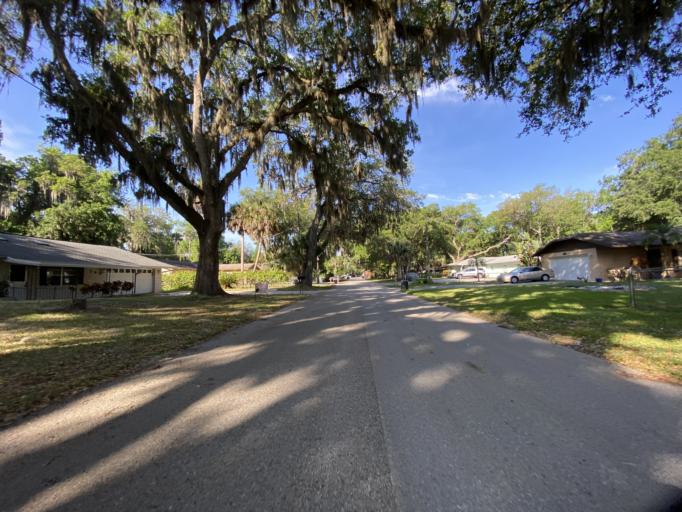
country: US
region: Florida
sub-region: Volusia County
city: South Daytona
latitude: 29.1757
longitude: -81.0199
